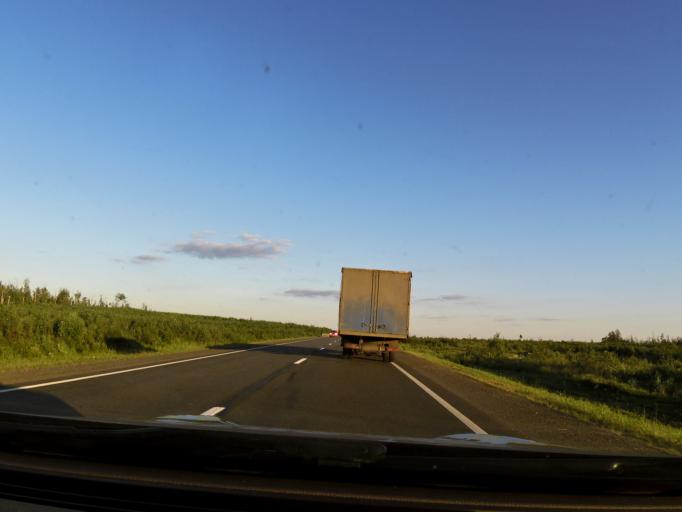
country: RU
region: Jaroslavl
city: Prechistoye
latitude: 58.6266
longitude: 40.3298
